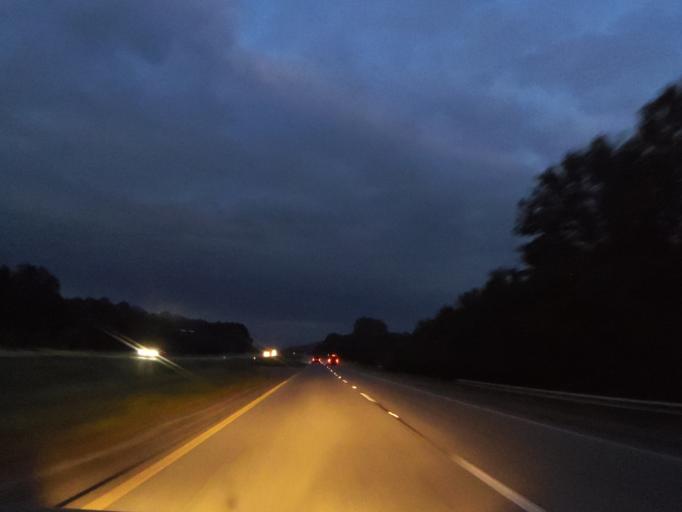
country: US
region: Alabama
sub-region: Jackson County
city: Scottsboro
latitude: 34.6226
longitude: -86.1801
